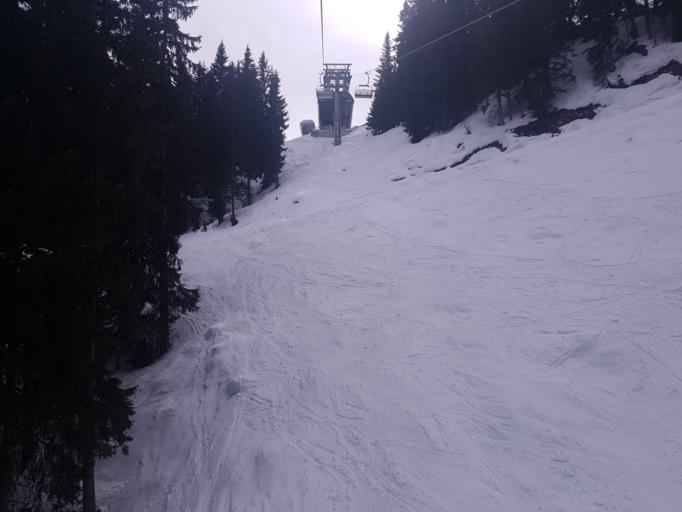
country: AT
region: Tyrol
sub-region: Politischer Bezirk Kufstein
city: Wildschoenau
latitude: 47.4330
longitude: 12.0827
